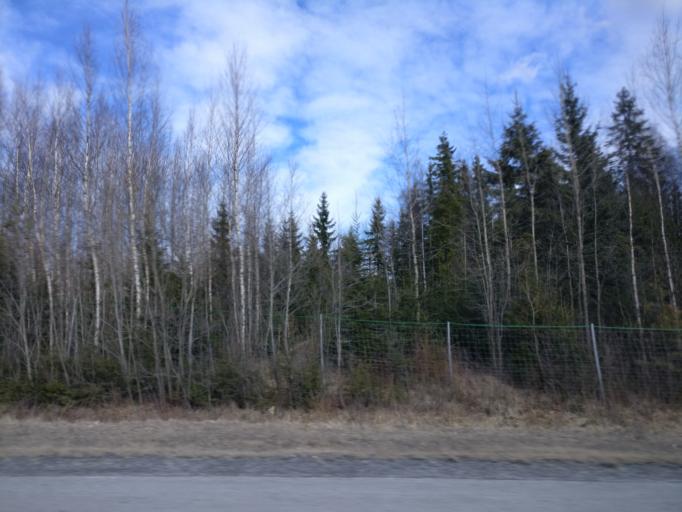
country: FI
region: Haeme
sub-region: Haemeenlinna
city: Parola
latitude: 61.0778
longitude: 24.2755
